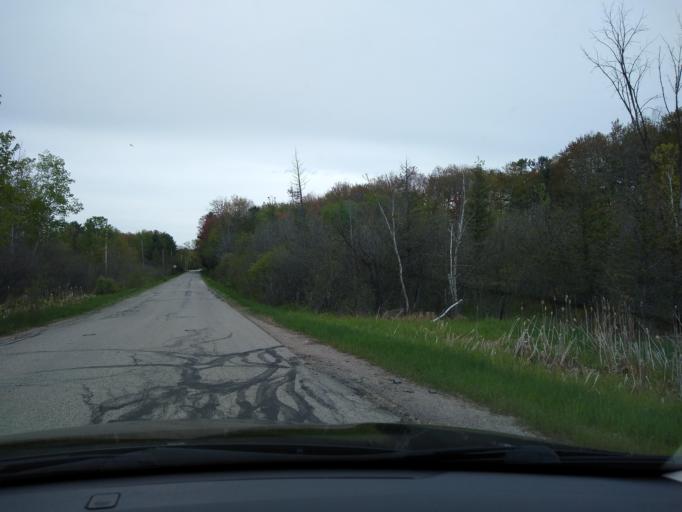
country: US
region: Michigan
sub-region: Delta County
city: Gladstone
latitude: 45.8910
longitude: -87.0656
